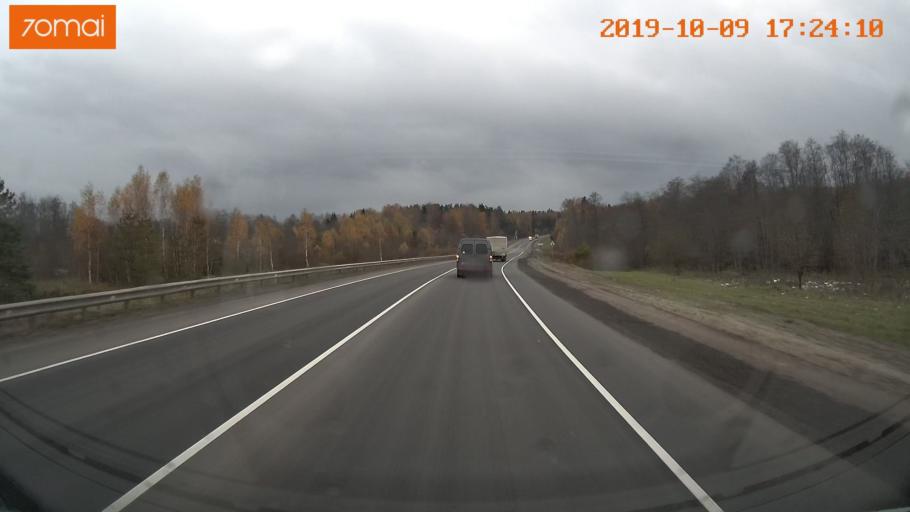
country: RU
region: Ivanovo
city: Furmanov
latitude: 57.1877
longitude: 41.1108
